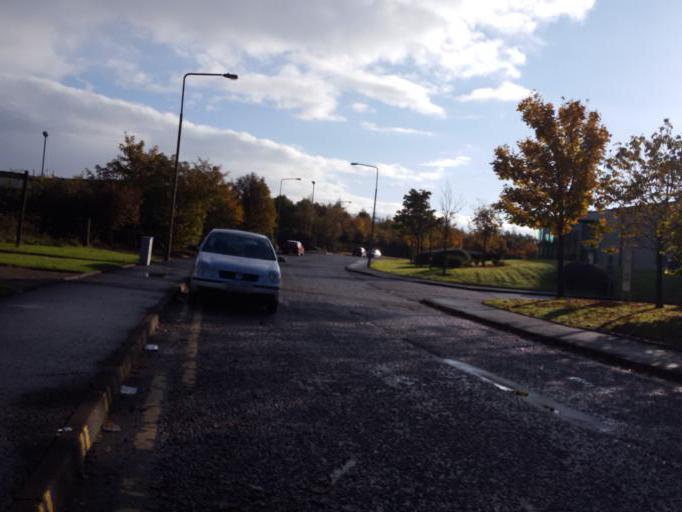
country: GB
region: Scotland
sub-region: West Lothian
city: West Calder
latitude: 55.8931
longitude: -3.5757
